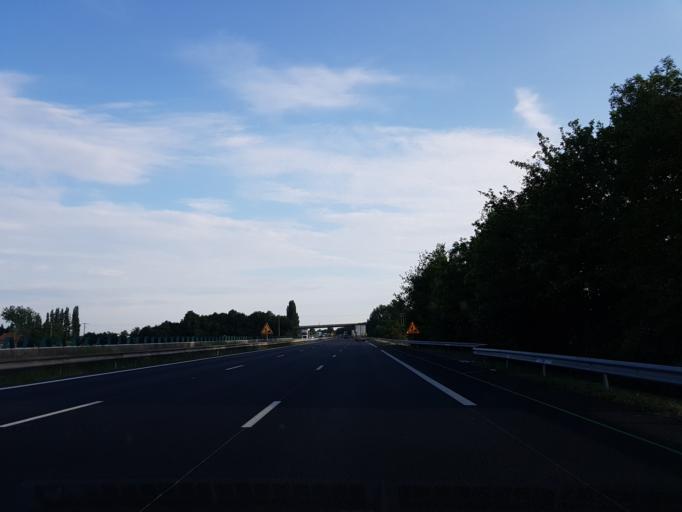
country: FR
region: Picardie
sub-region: Departement de la Somme
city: Roye
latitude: 49.6494
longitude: 2.7613
